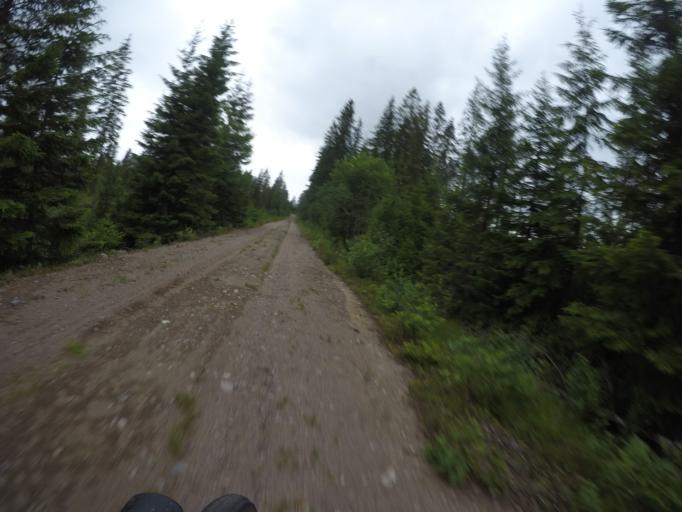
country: SE
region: OErebro
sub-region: Hallefors Kommun
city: Haellefors
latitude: 60.0256
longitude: 14.5683
